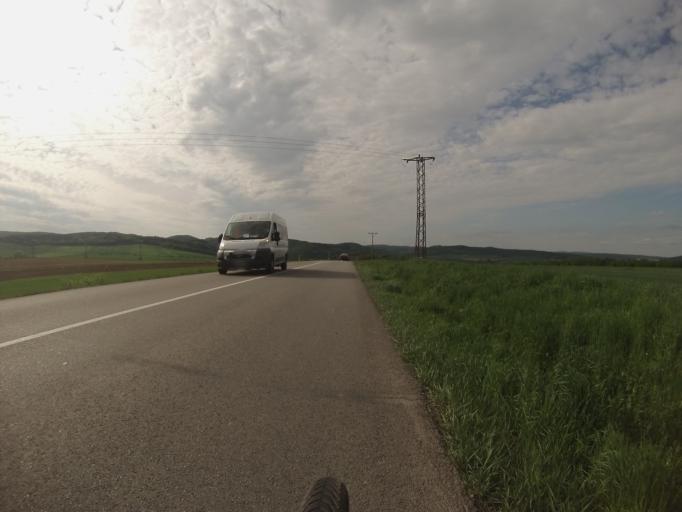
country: CZ
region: South Moravian
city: Veverska Bityska
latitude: 49.2582
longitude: 16.4471
